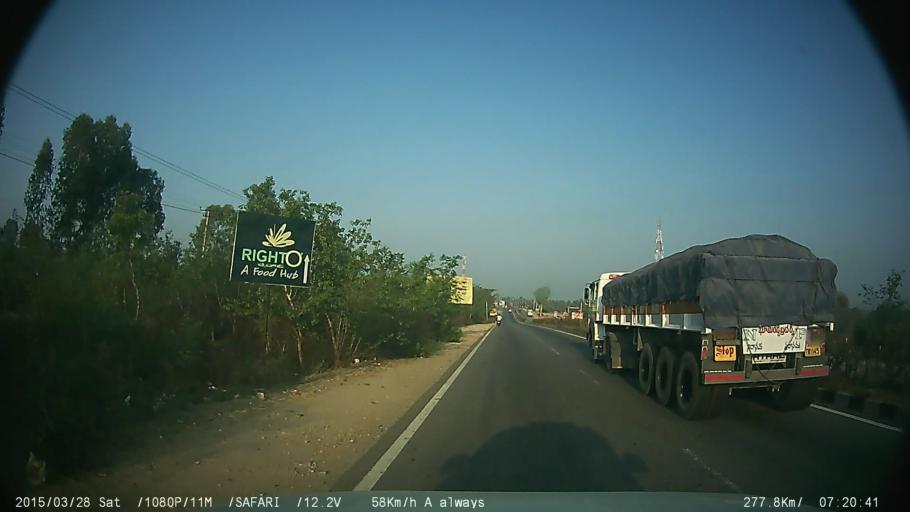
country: IN
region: Karnataka
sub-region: Mandya
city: Mandya
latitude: 12.4967
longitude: 76.8104
